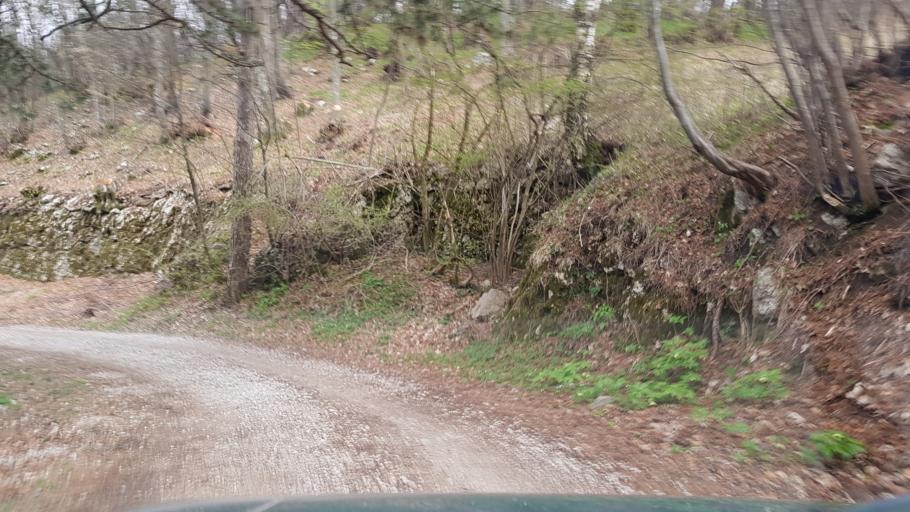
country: SI
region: Kanal
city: Deskle
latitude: 46.0669
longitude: 13.5628
